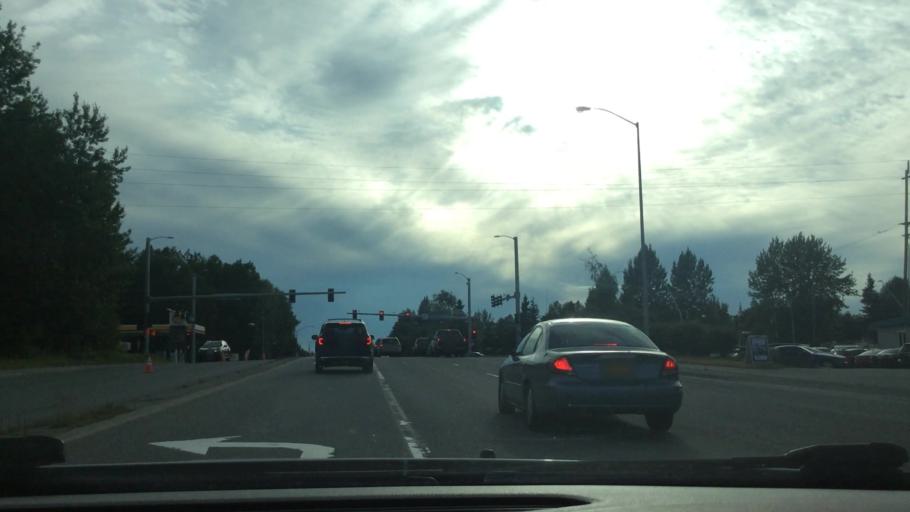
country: US
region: Alaska
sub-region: Anchorage Municipality
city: Anchorage
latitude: 61.1808
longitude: -149.8961
